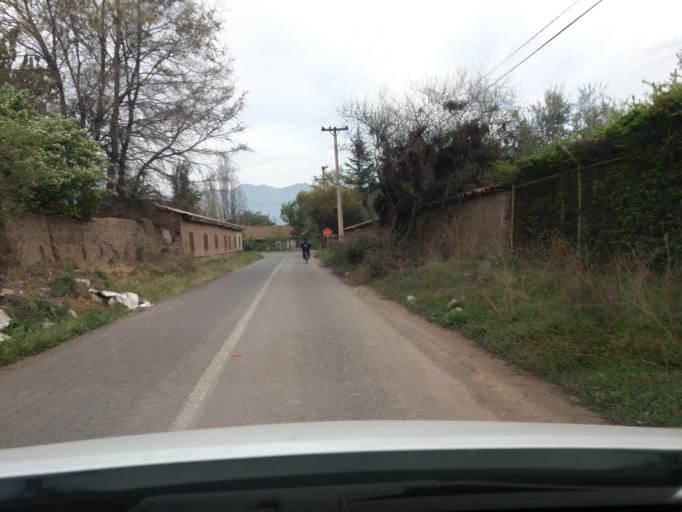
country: CL
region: Valparaiso
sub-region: Provincia de Los Andes
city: Los Andes
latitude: -32.8240
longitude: -70.6467
